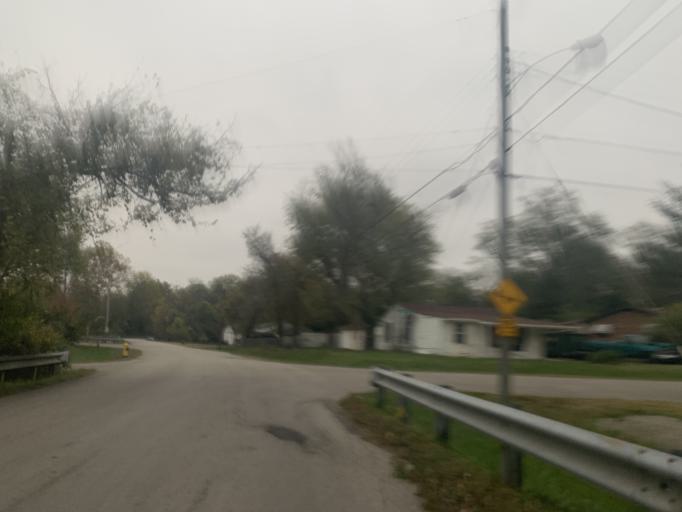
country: US
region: Kentucky
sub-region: Jefferson County
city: Saint Dennis
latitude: 38.2081
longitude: -85.8585
